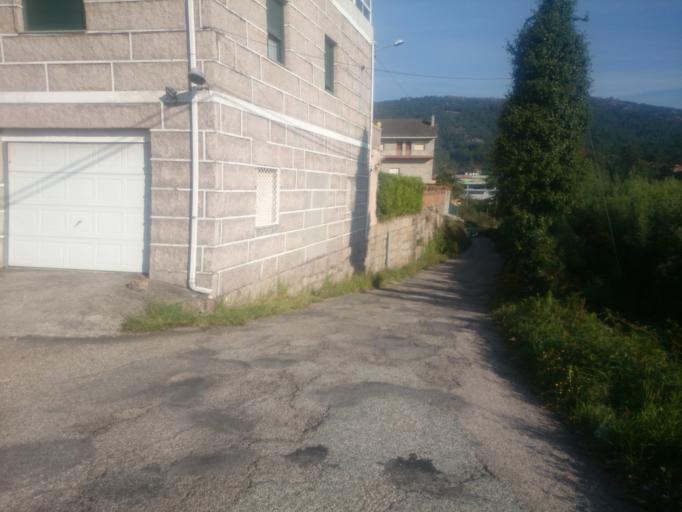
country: ES
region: Galicia
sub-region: Provincia de Pontevedra
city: Porrino
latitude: 42.1586
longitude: -8.6095
